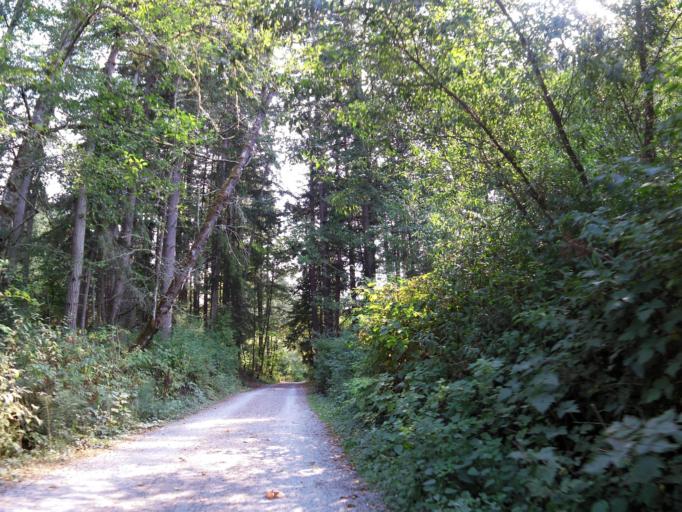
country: US
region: Washington
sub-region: Whatcom County
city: Bellingham
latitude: 48.7110
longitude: -122.4859
